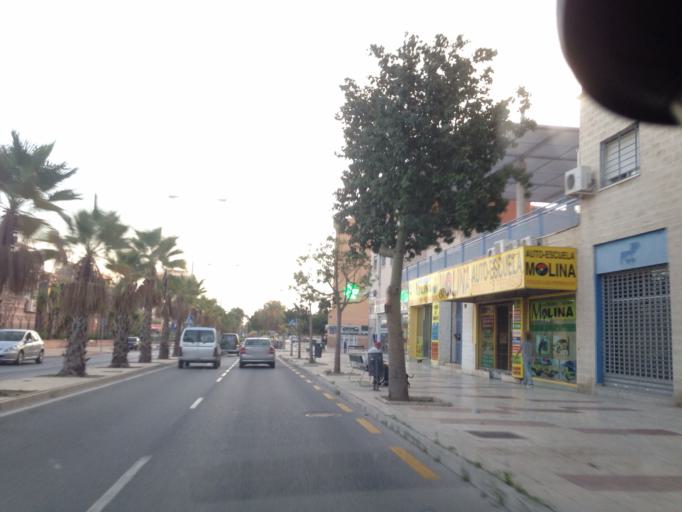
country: ES
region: Andalusia
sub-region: Provincia de Malaga
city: Malaga
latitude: 36.7354
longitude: -4.4334
